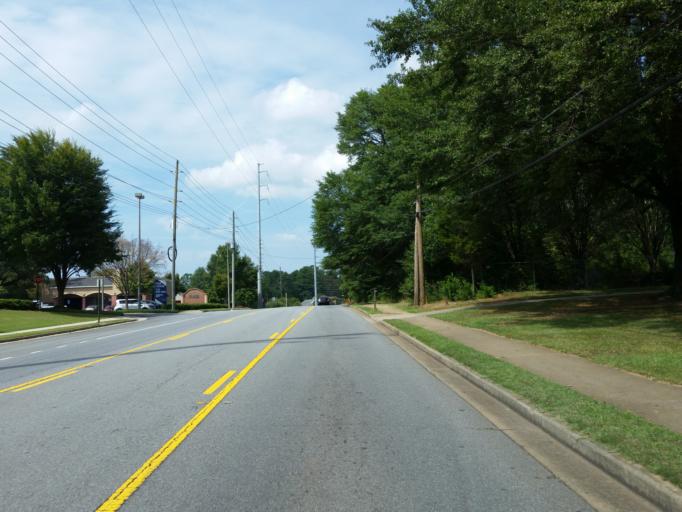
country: US
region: Georgia
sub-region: Cobb County
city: Marietta
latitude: 33.9931
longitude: -84.5077
